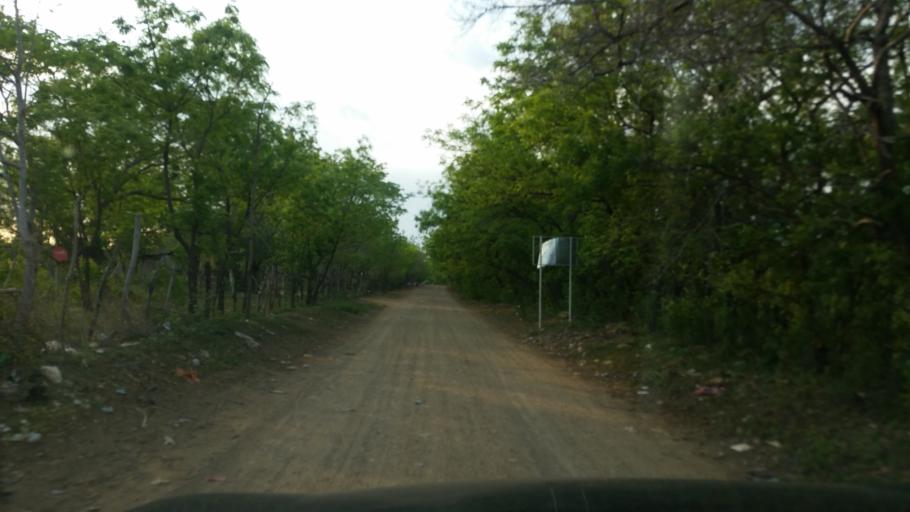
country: NI
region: Managua
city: Masachapa
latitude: 11.8100
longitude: -86.4842
